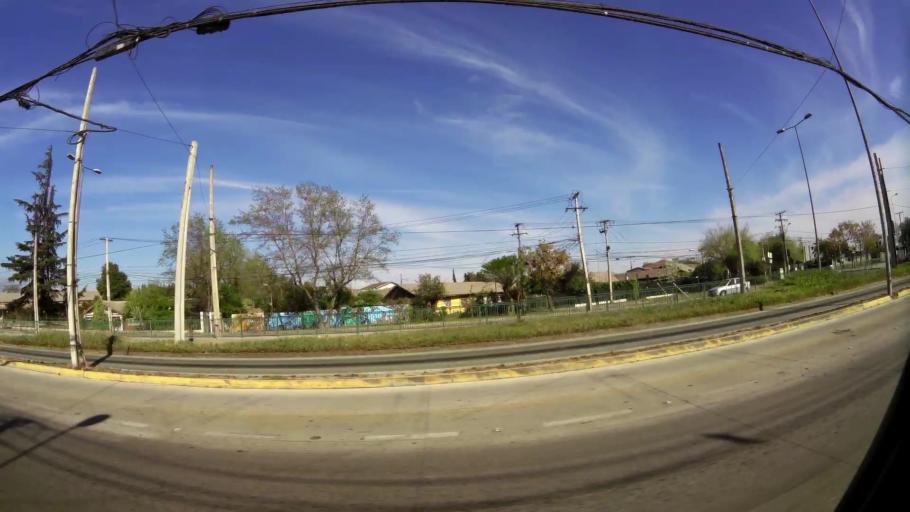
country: CL
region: Santiago Metropolitan
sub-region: Provincia de Santiago
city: Lo Prado
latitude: -33.5080
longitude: -70.7180
